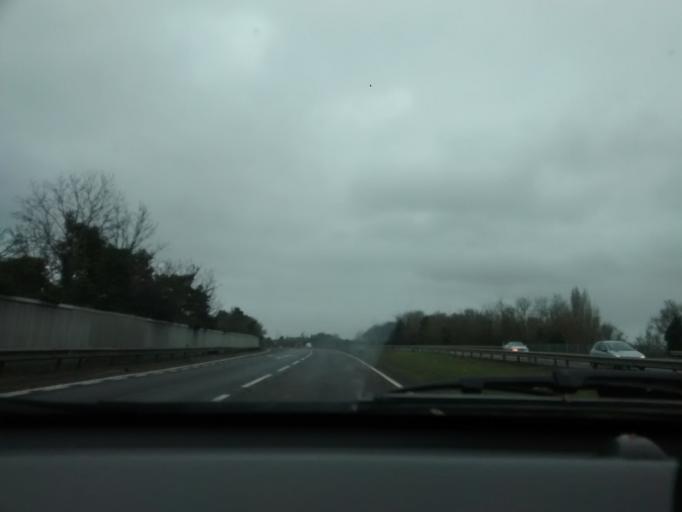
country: GB
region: England
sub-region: Suffolk
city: Bramford
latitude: 52.1088
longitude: 1.1063
